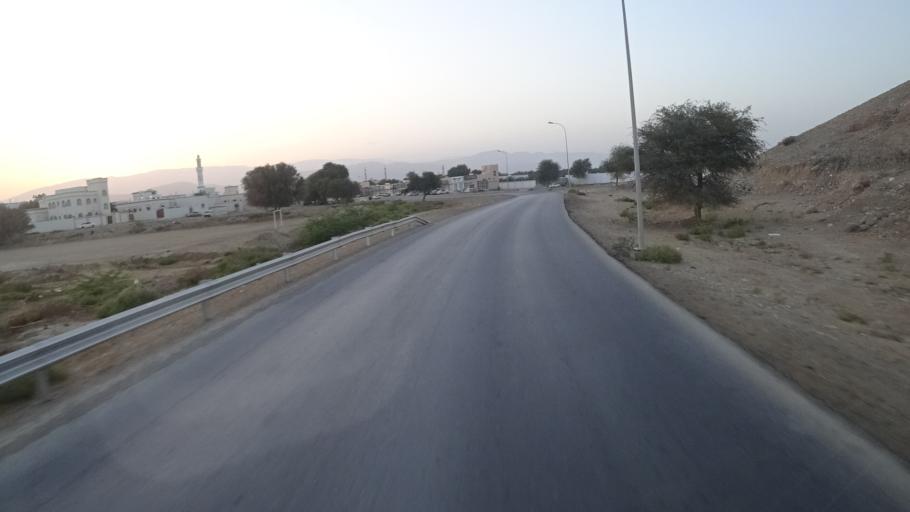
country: OM
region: Ash Sharqiyah
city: Sur
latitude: 22.5392
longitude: 59.4919
